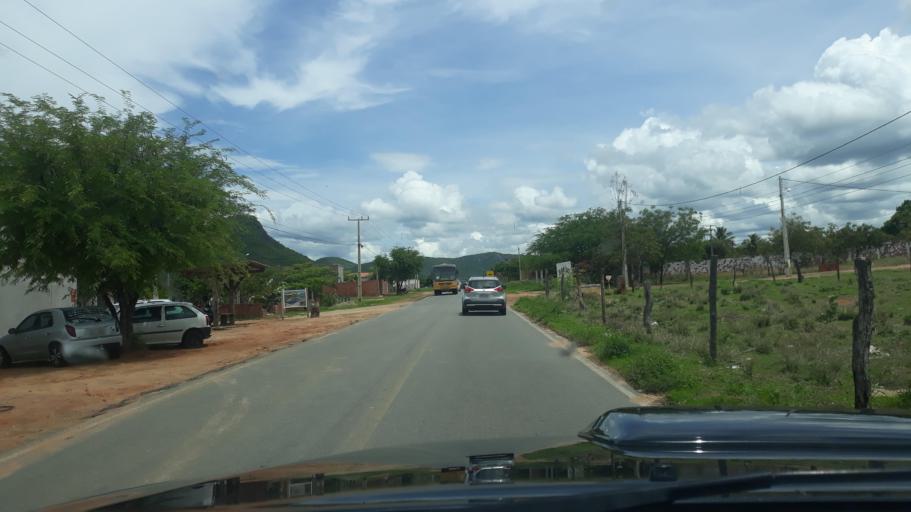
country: BR
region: Bahia
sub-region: Guanambi
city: Guanambi
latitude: -14.2677
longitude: -42.7158
